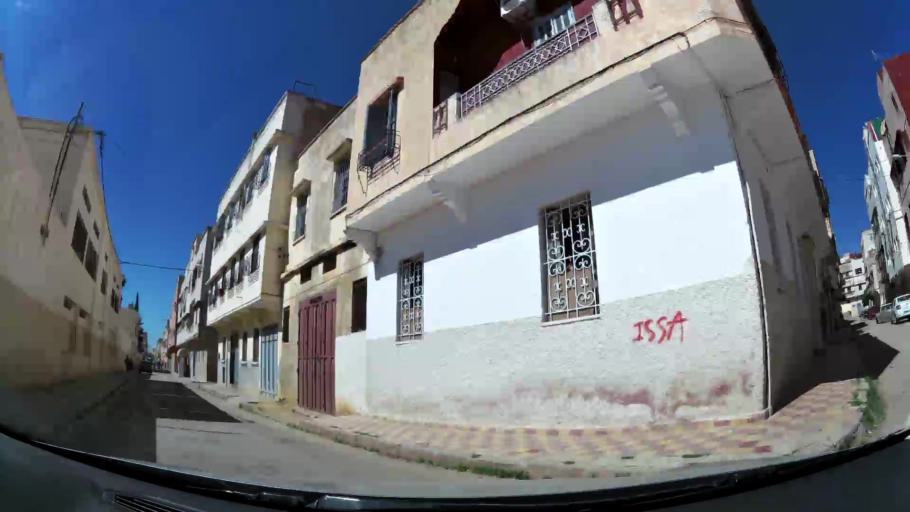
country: MA
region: Meknes-Tafilalet
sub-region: Meknes
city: Meknes
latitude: 33.8867
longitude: -5.5718
